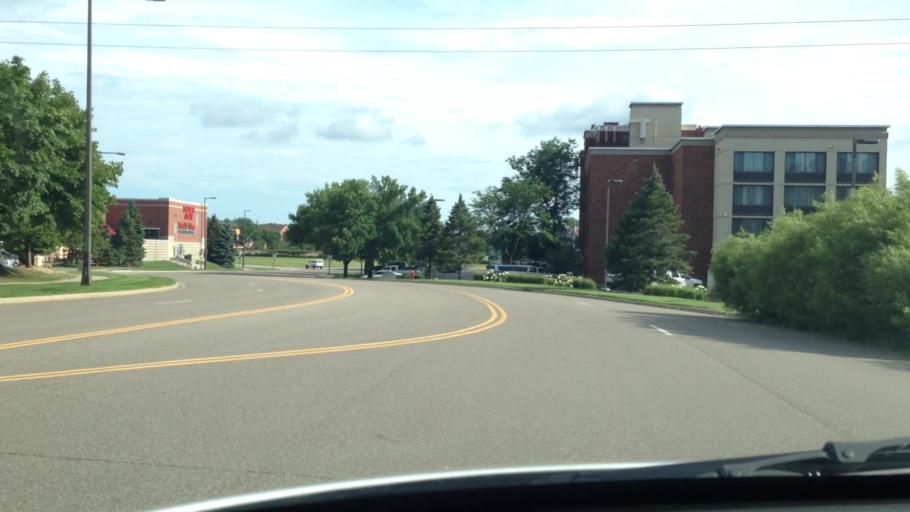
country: US
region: Minnesota
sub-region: Hennepin County
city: Edina
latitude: 44.8605
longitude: -93.3339
